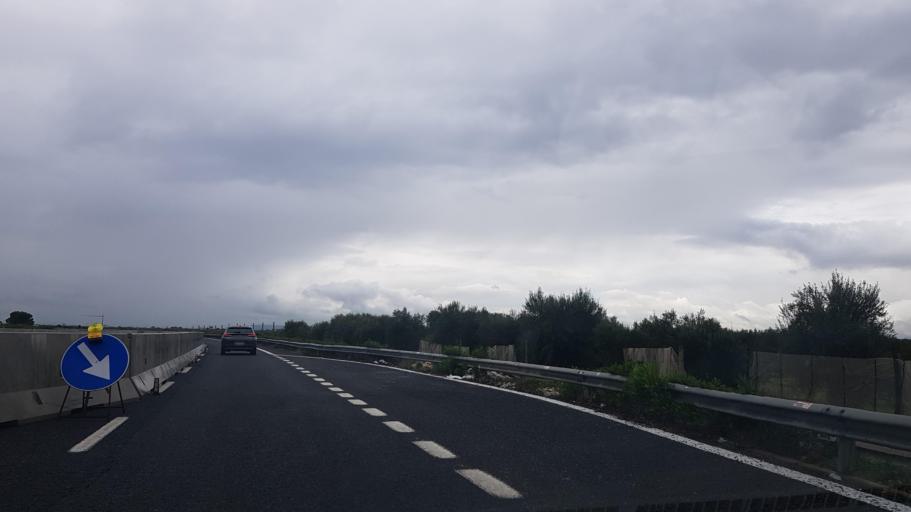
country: IT
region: Apulia
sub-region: Provincia di Taranto
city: Massafra
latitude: 40.5308
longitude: 17.1124
